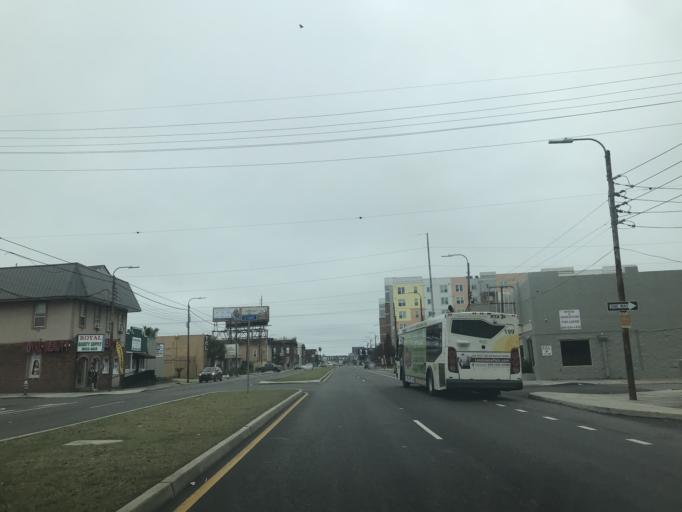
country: US
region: Louisiana
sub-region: Orleans Parish
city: New Orleans
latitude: 29.9658
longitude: -90.0993
